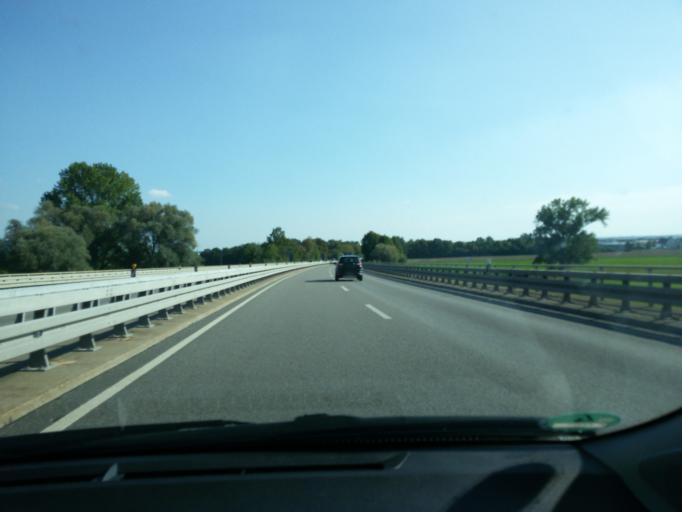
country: DE
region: Bavaria
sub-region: Swabia
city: Donauwoerth
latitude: 48.7112
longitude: 10.8025
